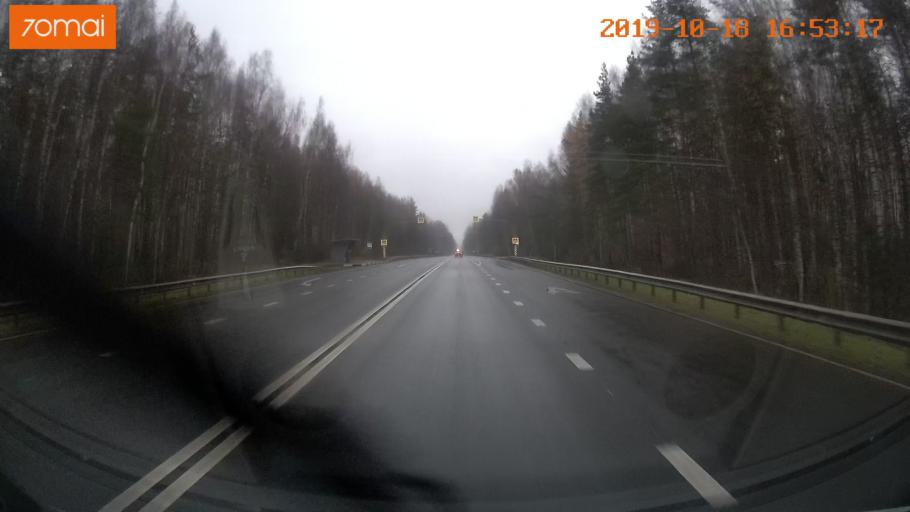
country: RU
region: Ivanovo
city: Nerl'
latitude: 56.6127
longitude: 40.5588
